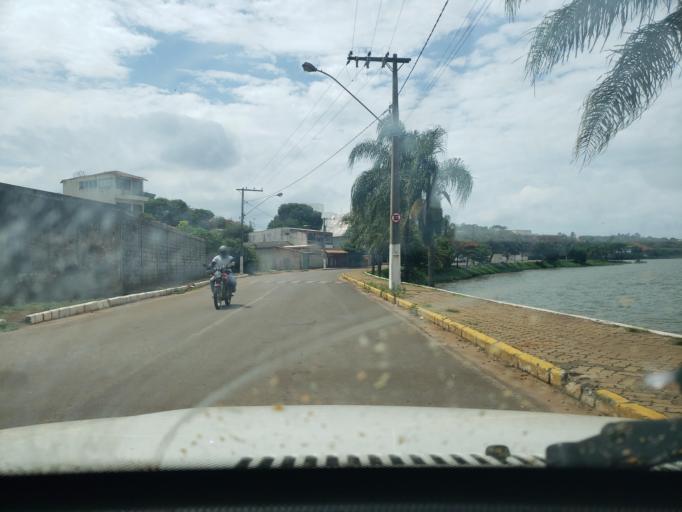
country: BR
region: Minas Gerais
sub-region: Boa Esperanca
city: Boa Esperanca
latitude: -21.0863
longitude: -45.5704
